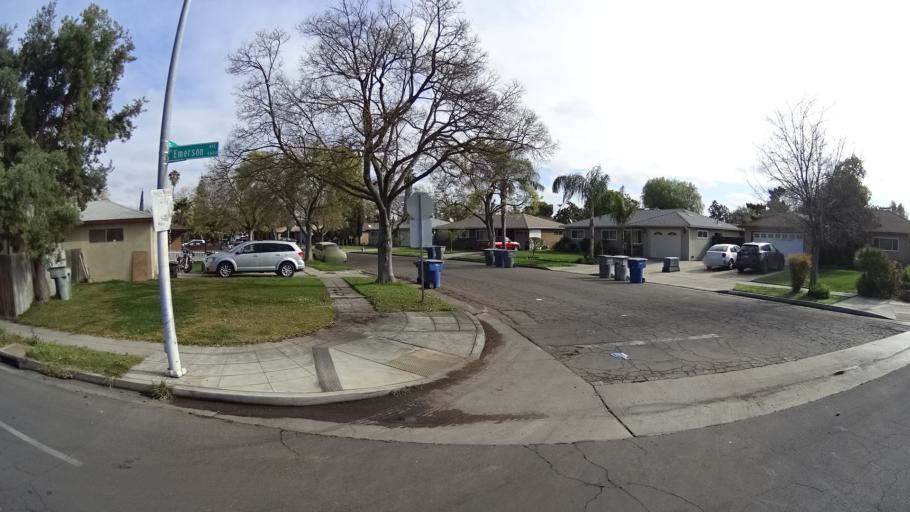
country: US
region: California
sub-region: Fresno County
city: West Park
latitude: 36.8046
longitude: -119.8509
